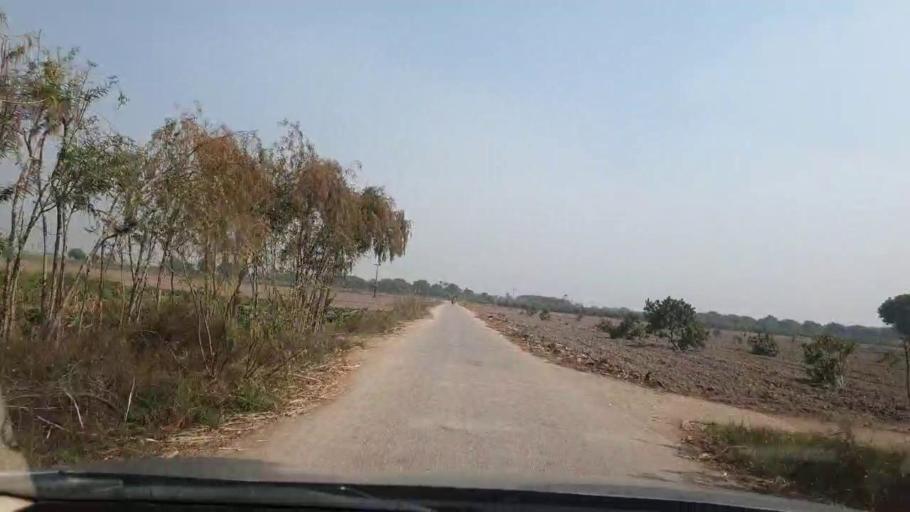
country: PK
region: Sindh
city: Tando Allahyar
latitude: 25.4888
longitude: 68.7933
